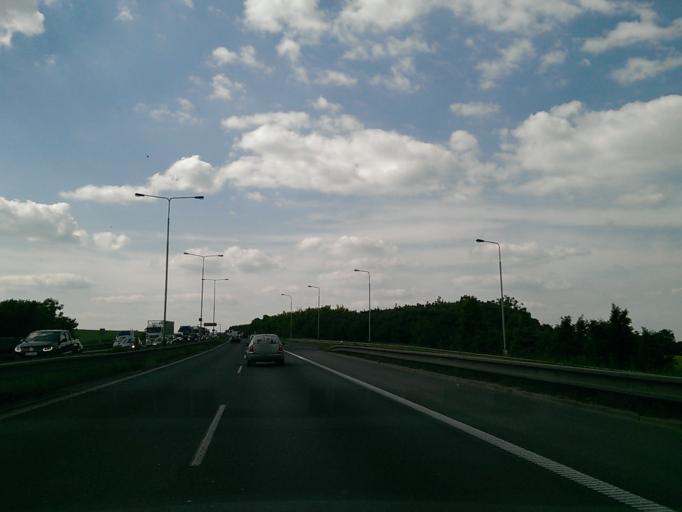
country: CZ
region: Central Bohemia
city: Zdiby
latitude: 50.1590
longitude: 14.4823
